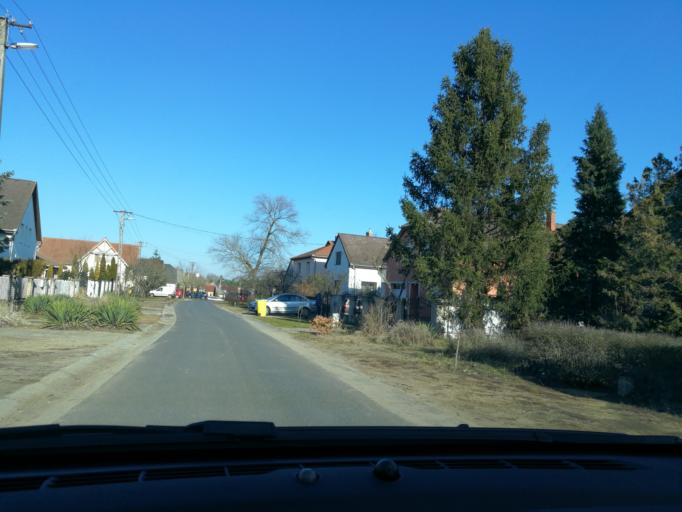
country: HU
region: Szabolcs-Szatmar-Bereg
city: Nyiregyhaza
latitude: 47.9255
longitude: 21.7600
